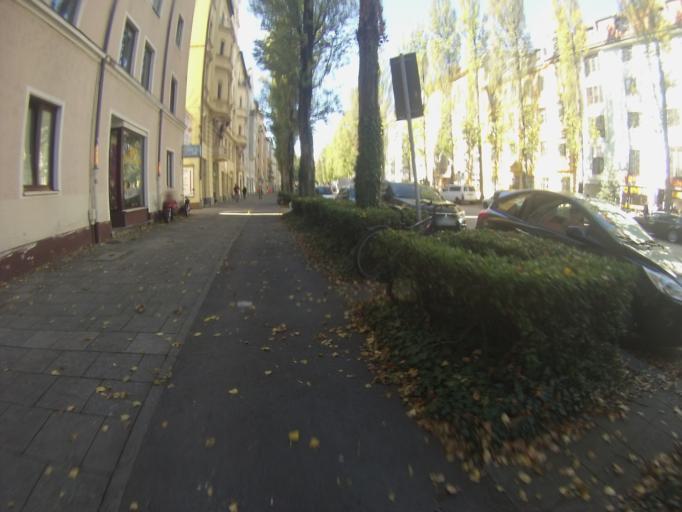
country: DE
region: Bavaria
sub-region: Upper Bavaria
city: Munich
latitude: 48.1237
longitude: 11.5474
